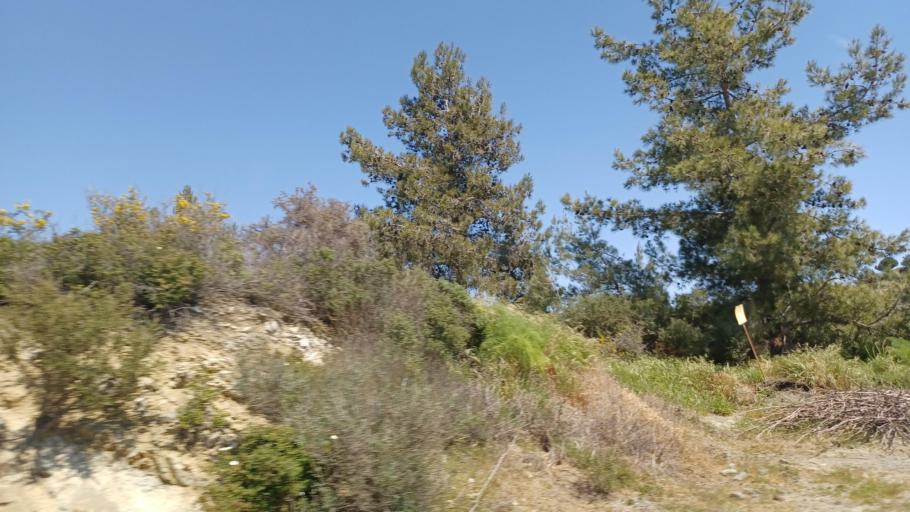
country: CY
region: Limassol
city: Parekklisha
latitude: 34.8085
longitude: 33.1628
